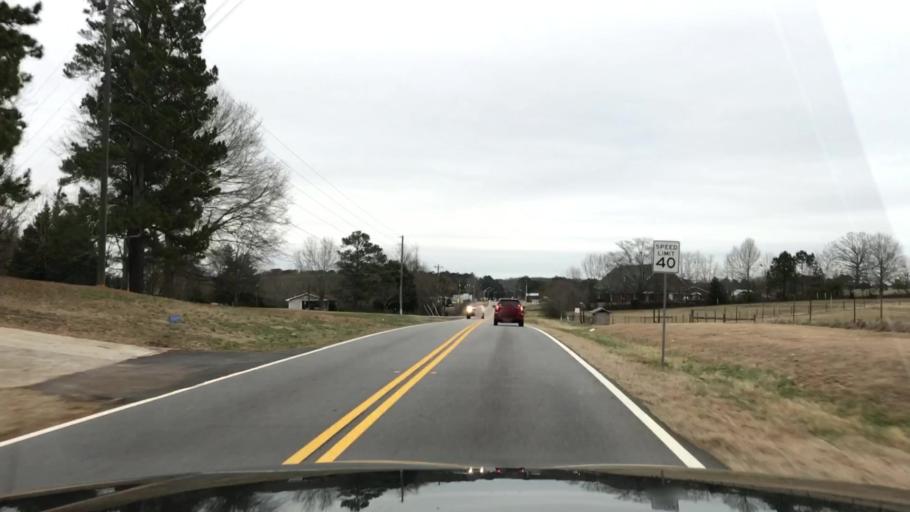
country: US
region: Georgia
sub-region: Walton County
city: Loganville
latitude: 33.9031
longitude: -83.8086
